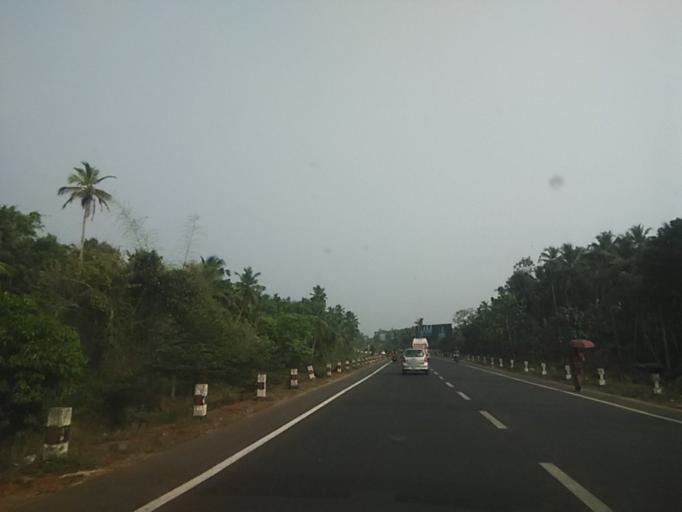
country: IN
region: Kerala
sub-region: Kozhikode
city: Kozhikode
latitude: 11.3136
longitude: 75.7811
